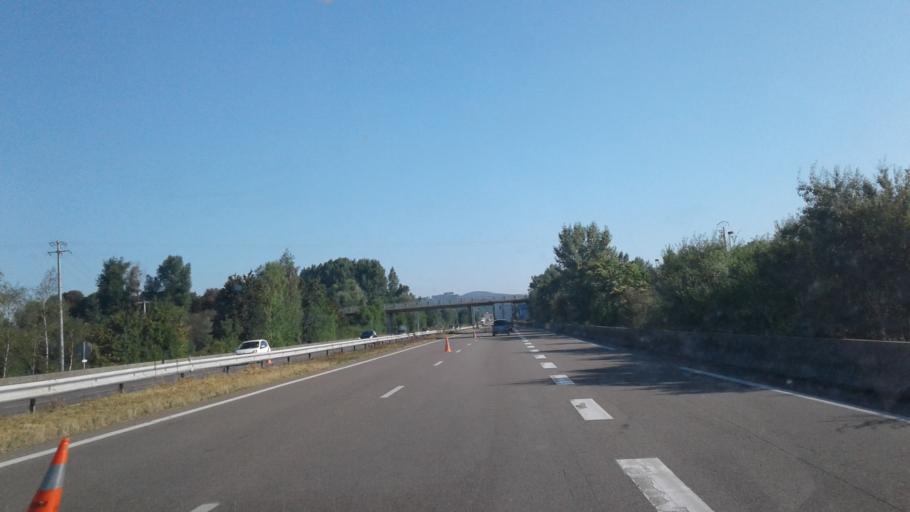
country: FR
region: Rhone-Alpes
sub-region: Departement de l'Ain
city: Saint-Martin-du-Mont
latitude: 46.0472
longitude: 5.3256
